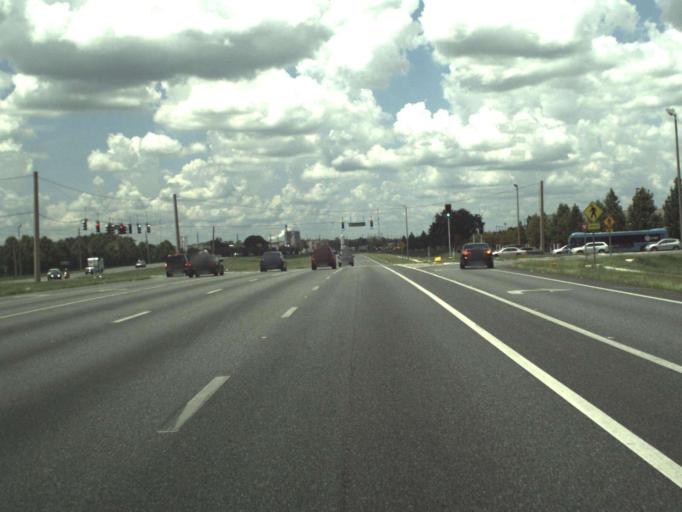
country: US
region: Florida
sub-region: Orange County
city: Fairview Shores
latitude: 28.5688
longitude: -81.4149
